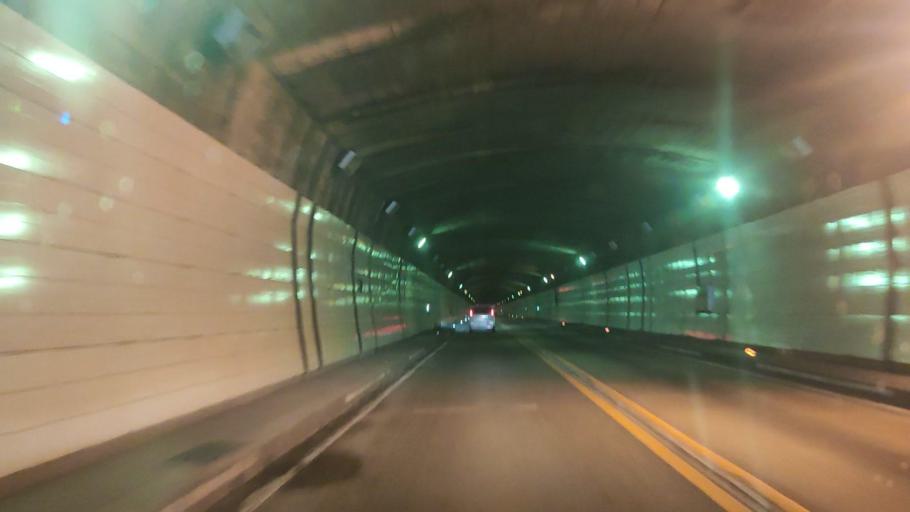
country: JP
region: Kumamoto
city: Hitoyoshi
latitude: 32.1043
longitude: 130.8051
